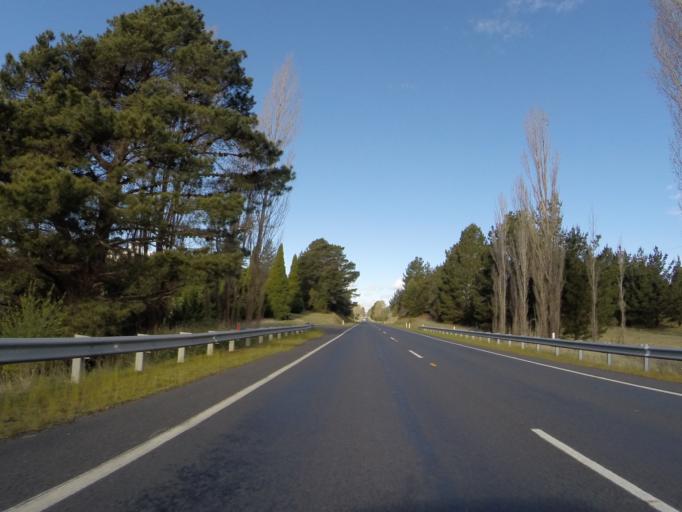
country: AU
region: New South Wales
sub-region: Wingecarribee
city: Moss Vale
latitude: -34.5681
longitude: 150.4304
